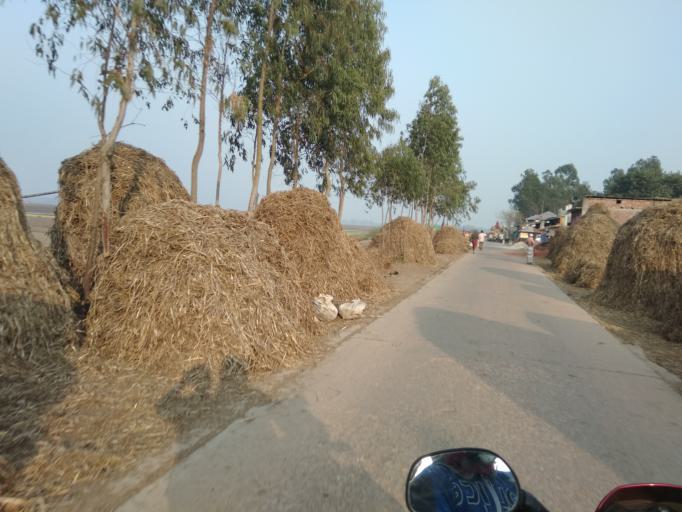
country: BD
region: Rajshahi
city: Ishurdi
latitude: 24.4808
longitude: 89.2344
